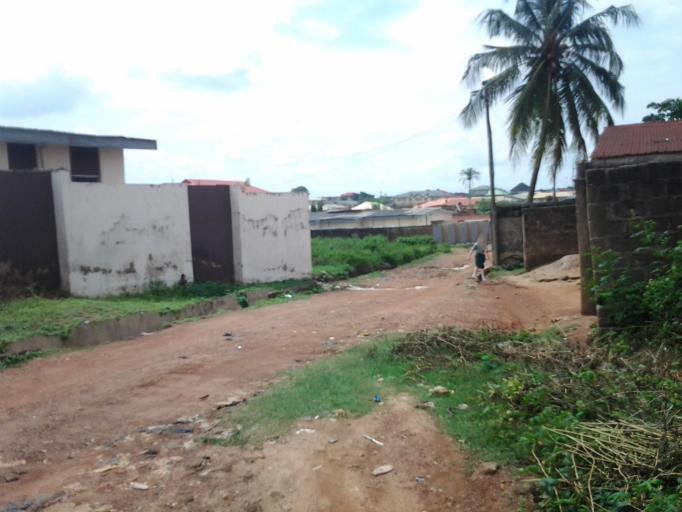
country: NG
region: Oyo
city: Ibadan
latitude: 7.4351
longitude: 3.9529
